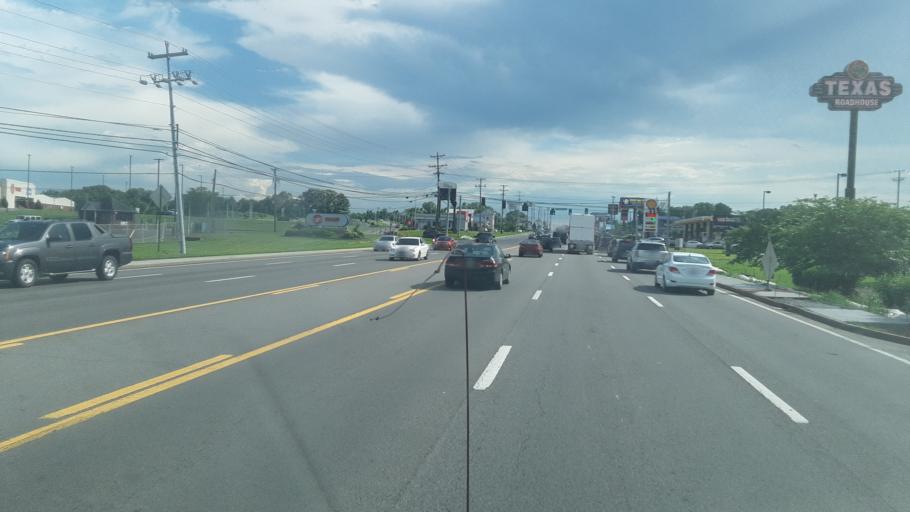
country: US
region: Tennessee
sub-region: Montgomery County
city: Clarksville
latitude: 36.5835
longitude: -87.2965
